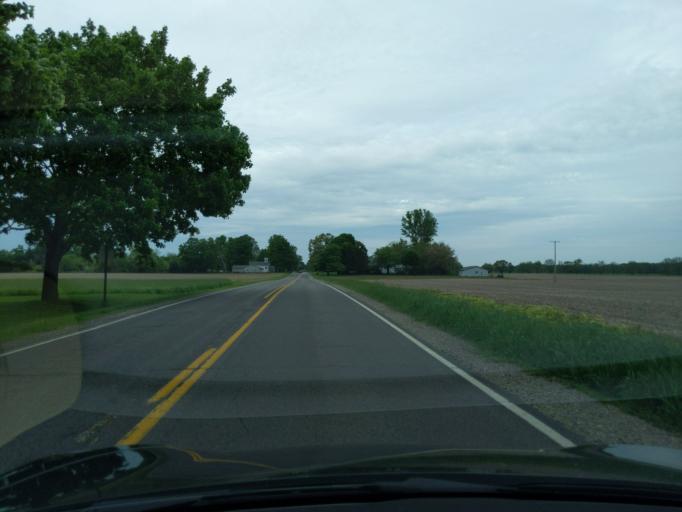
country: US
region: Michigan
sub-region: Ingham County
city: Leslie
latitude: 42.4841
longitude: -84.3562
